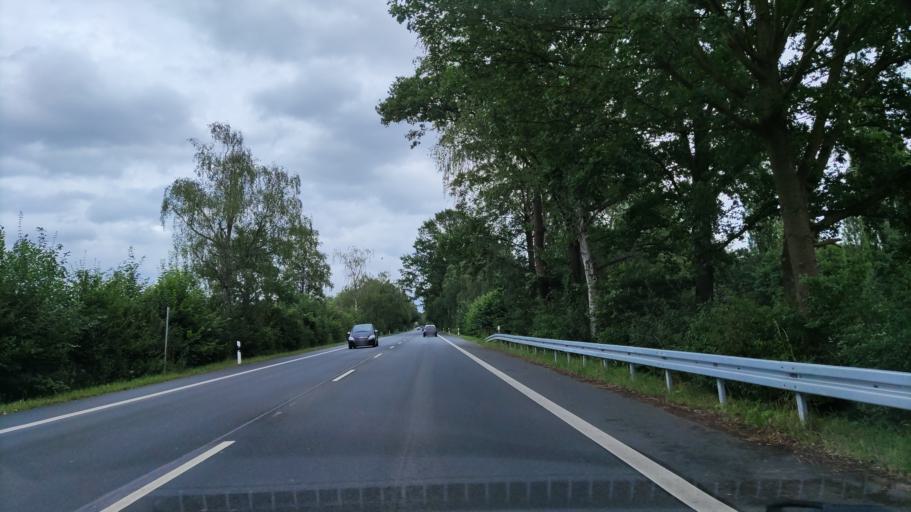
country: DE
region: North Rhine-Westphalia
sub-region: Regierungsbezirk Arnsberg
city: Hamm
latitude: 51.6715
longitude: 7.8560
